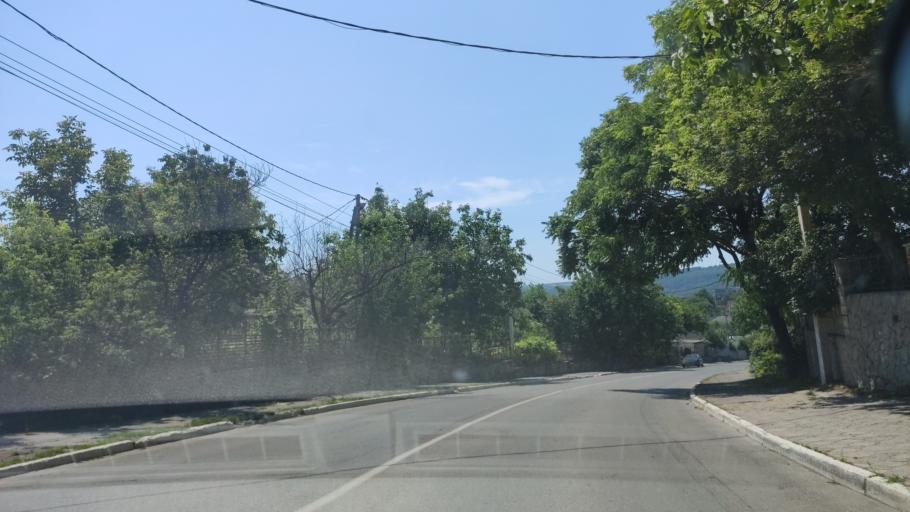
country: MD
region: Raionul Soroca
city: Soroca
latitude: 48.1655
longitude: 28.3048
